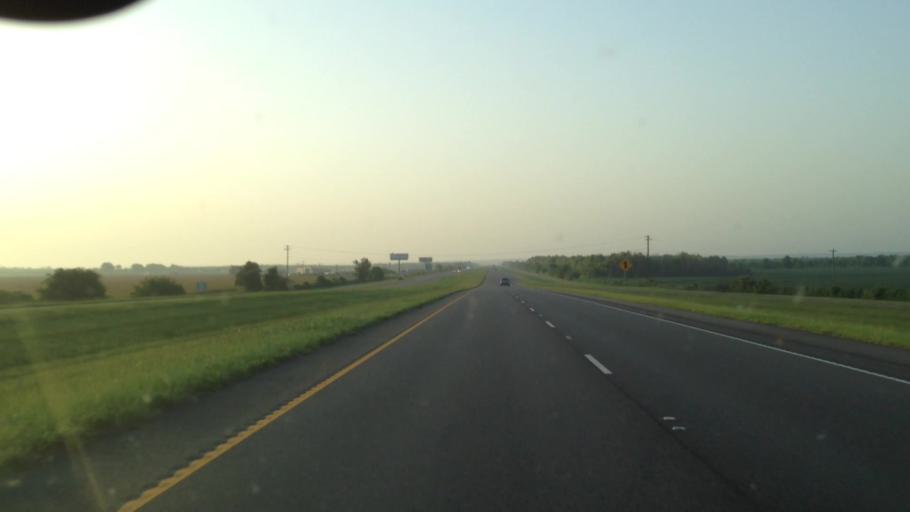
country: US
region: Louisiana
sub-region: Natchitoches Parish
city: Campti
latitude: 31.8373
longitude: -93.2752
